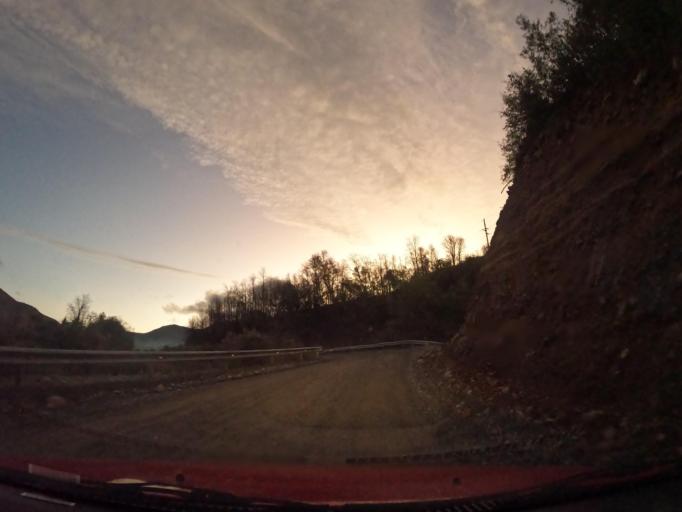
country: CL
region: Maule
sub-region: Provincia de Linares
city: Colbun
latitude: -35.8578
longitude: -71.2311
